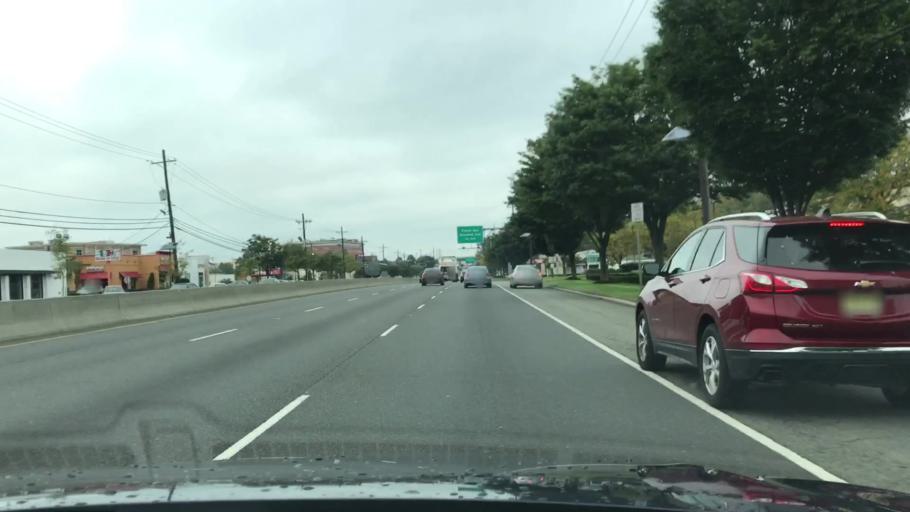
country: US
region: New Jersey
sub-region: Bergen County
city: River Edge
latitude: 40.9140
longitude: -74.0464
